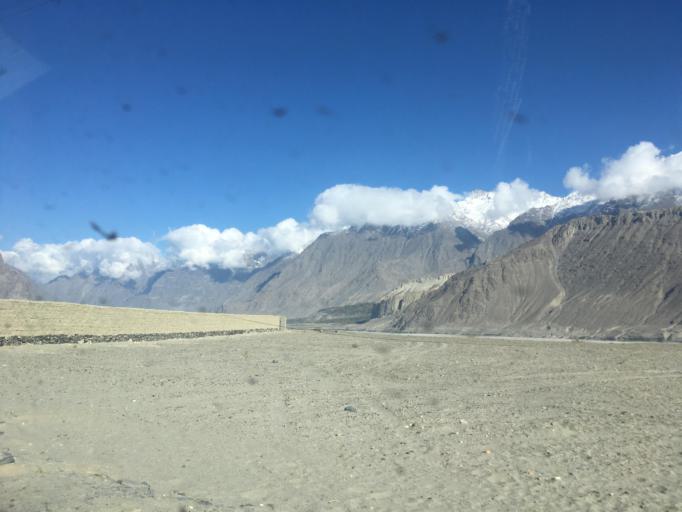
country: PK
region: Gilgit-Baltistan
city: Skardu
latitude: 35.3590
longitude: 75.5352
